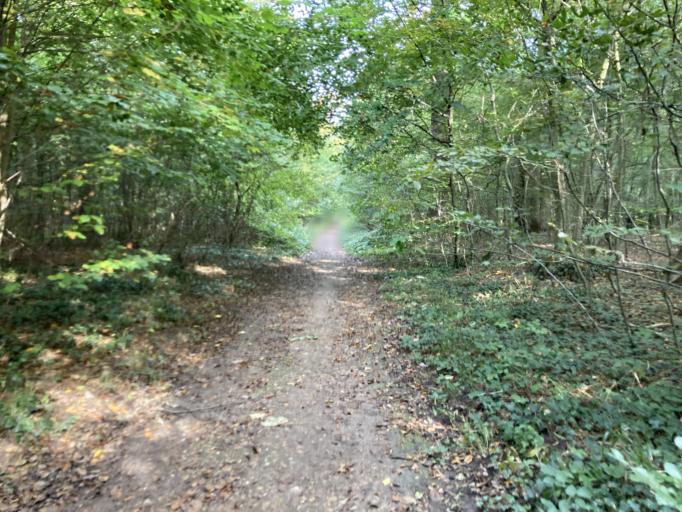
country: FR
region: Ile-de-France
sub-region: Departement des Yvelines
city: Saint-Germain-en-Laye
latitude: 48.9229
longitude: 2.0963
